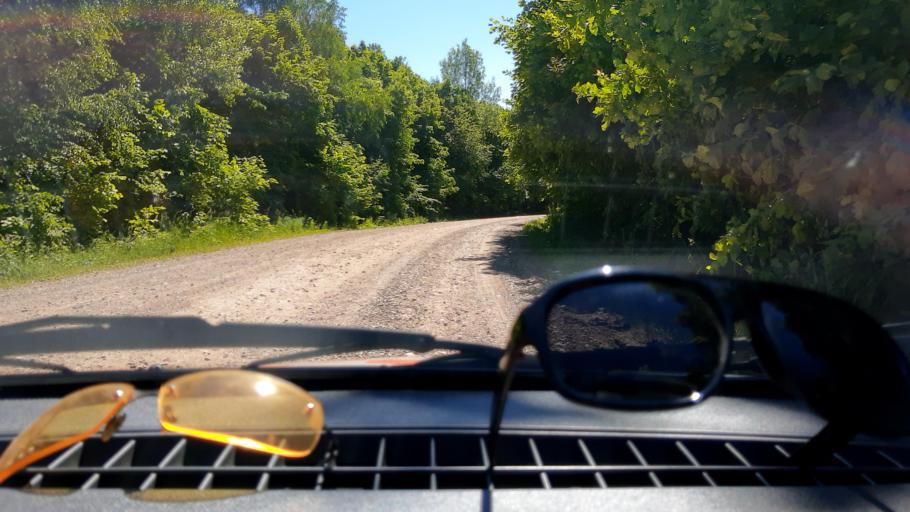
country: RU
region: Bashkortostan
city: Ulu-Telyak
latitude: 54.8020
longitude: 57.0319
